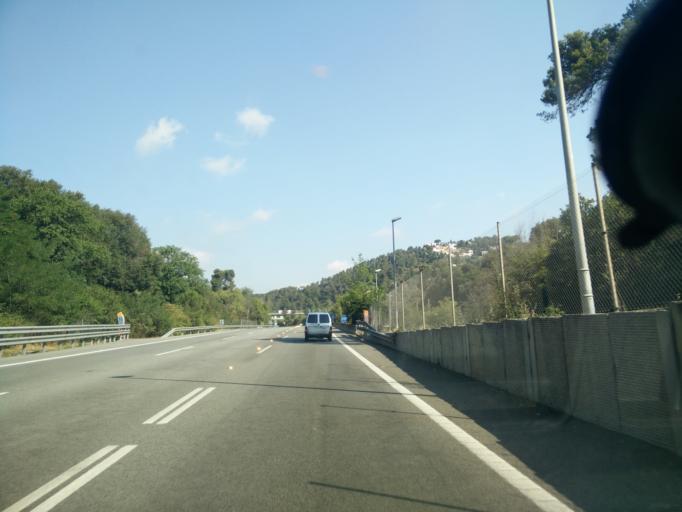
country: ES
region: Catalonia
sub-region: Provincia de Barcelona
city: Sant Just Desvern
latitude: 41.4237
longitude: 2.0933
